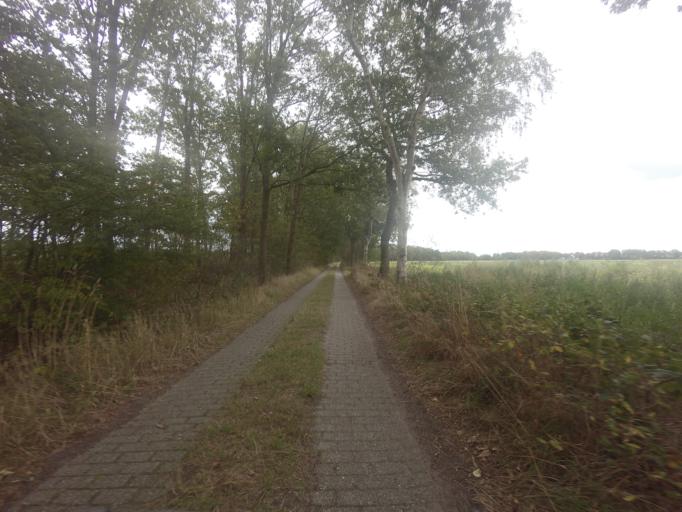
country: NL
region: Friesland
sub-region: Gemeente Weststellingwerf
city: Noordwolde
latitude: 52.9332
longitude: 6.1728
